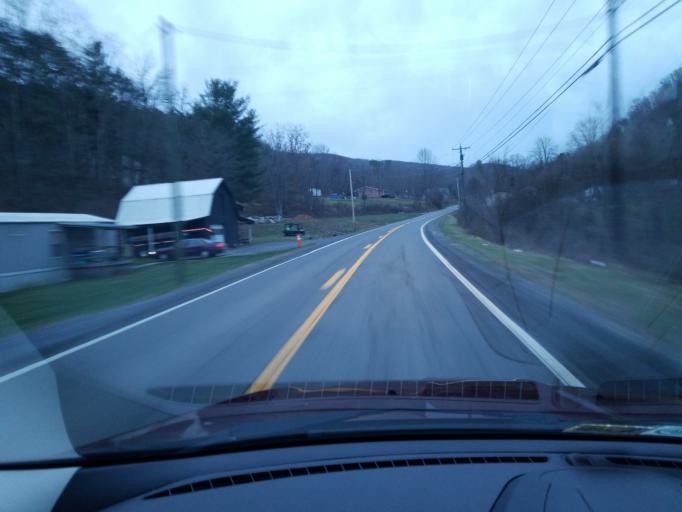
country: US
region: West Virginia
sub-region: Greenbrier County
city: Lewisburg
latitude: 37.7697
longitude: -80.3940
